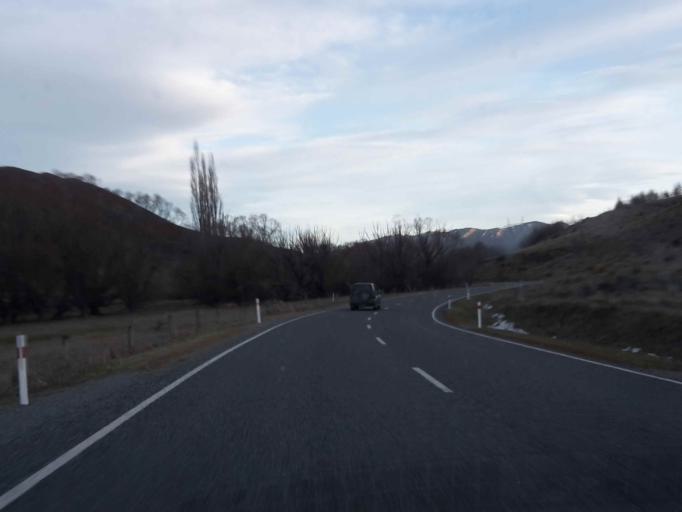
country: NZ
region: Canterbury
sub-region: Timaru District
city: Pleasant Point
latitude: -44.0629
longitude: 170.6736
